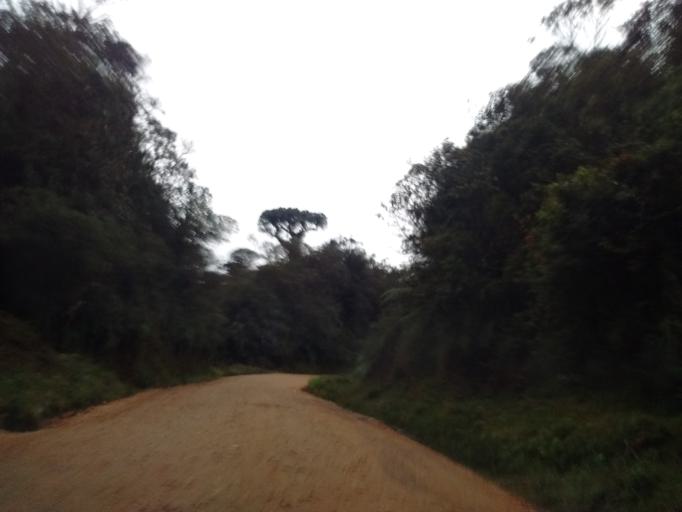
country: CO
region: Huila
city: Isnos
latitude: 2.1384
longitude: -76.3825
